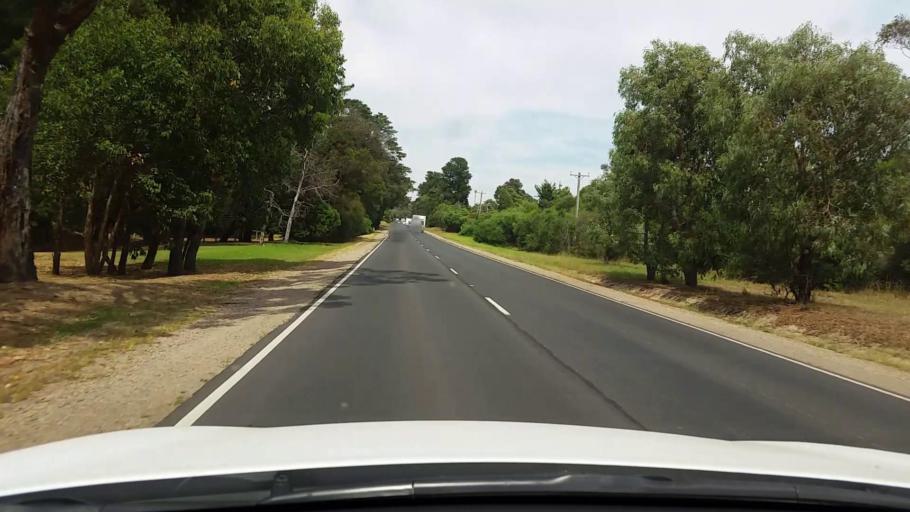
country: AU
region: Victoria
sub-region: Mornington Peninsula
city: Balnarring
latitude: -38.3687
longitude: 145.1342
